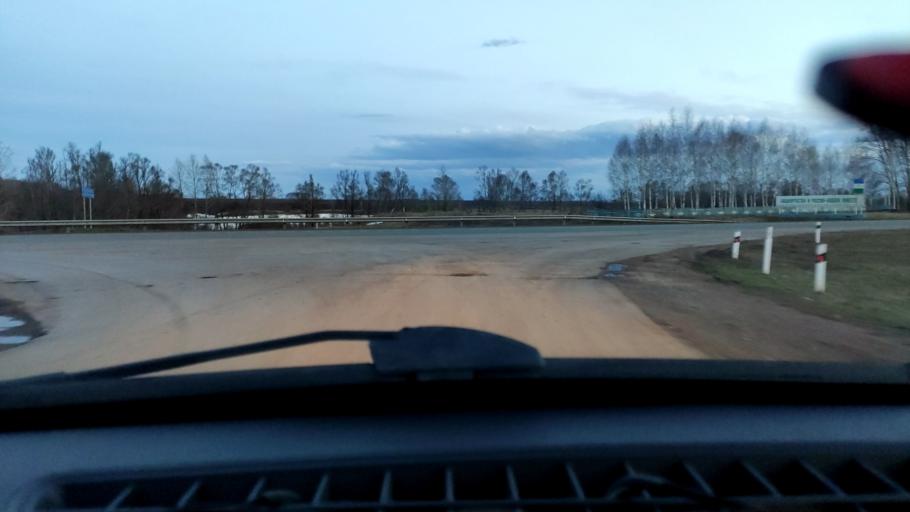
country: RU
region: Bashkortostan
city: Ulukulevo
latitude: 54.4176
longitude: 56.3432
